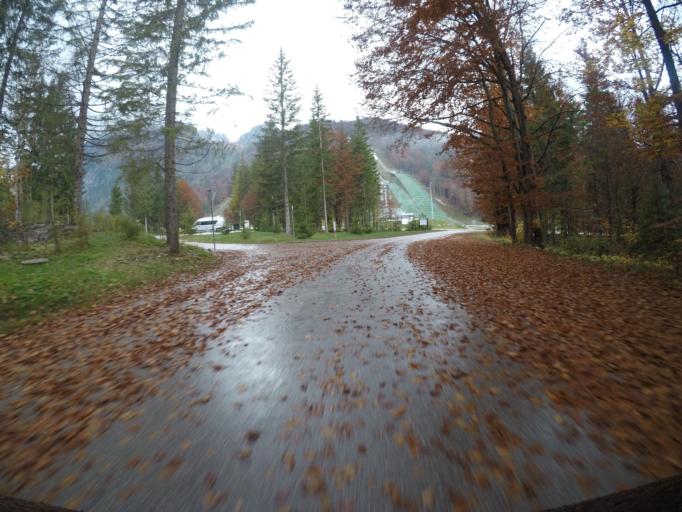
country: SI
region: Kranjska Gora
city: Kranjska Gora
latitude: 46.4780
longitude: 13.7256
